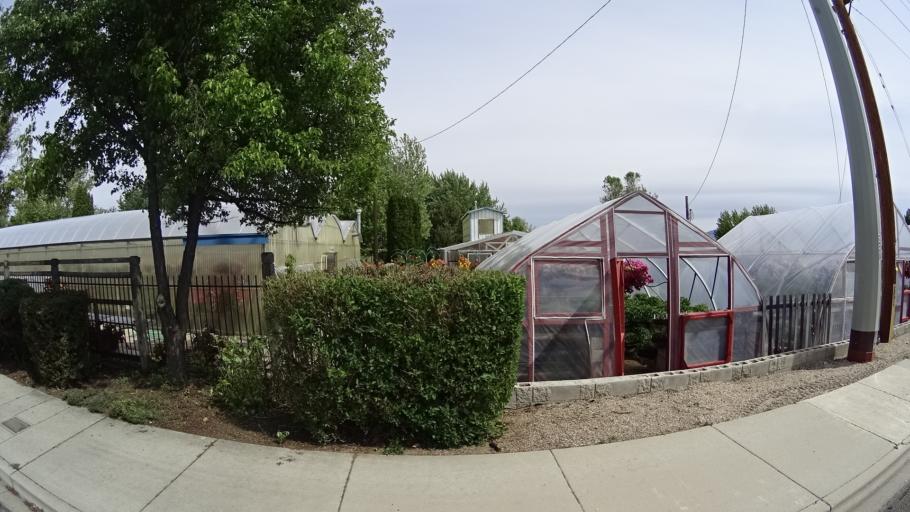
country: US
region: Idaho
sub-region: Ada County
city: Meridian
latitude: 43.5758
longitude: -116.3133
